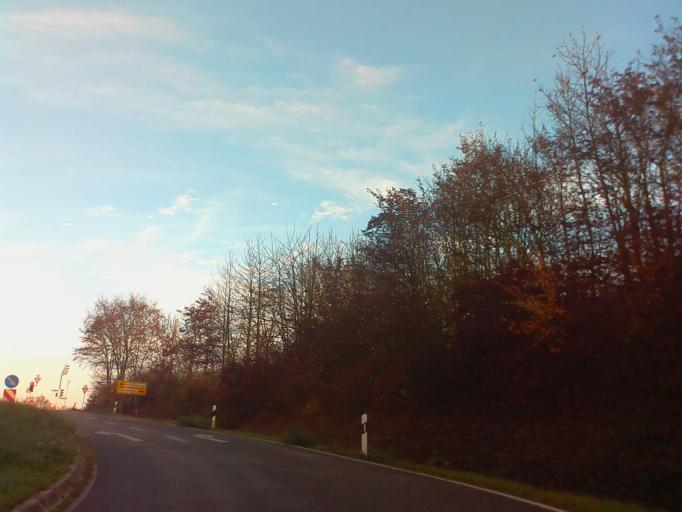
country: DE
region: Baden-Wuerttemberg
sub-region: Karlsruhe Region
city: Ilvesheim
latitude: 49.4976
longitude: 8.5379
